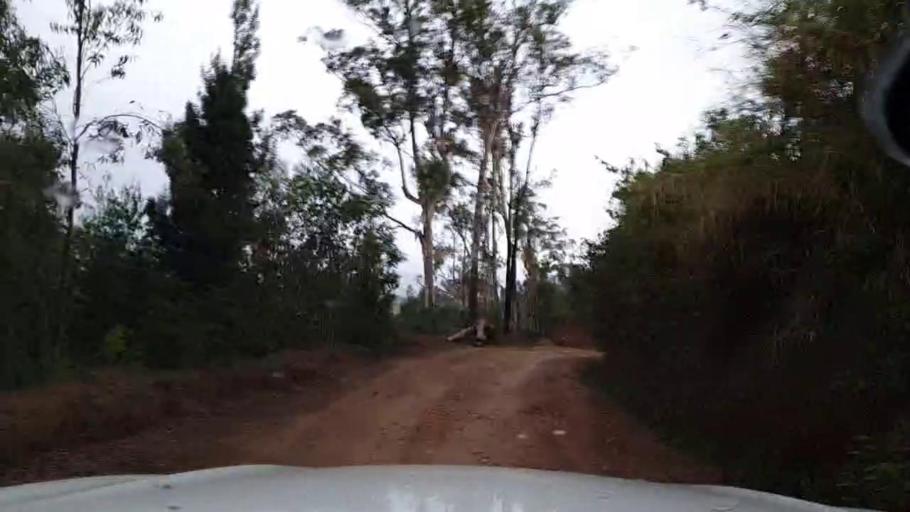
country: BI
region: Kayanza
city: Kayanza
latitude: -2.7858
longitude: 29.5316
